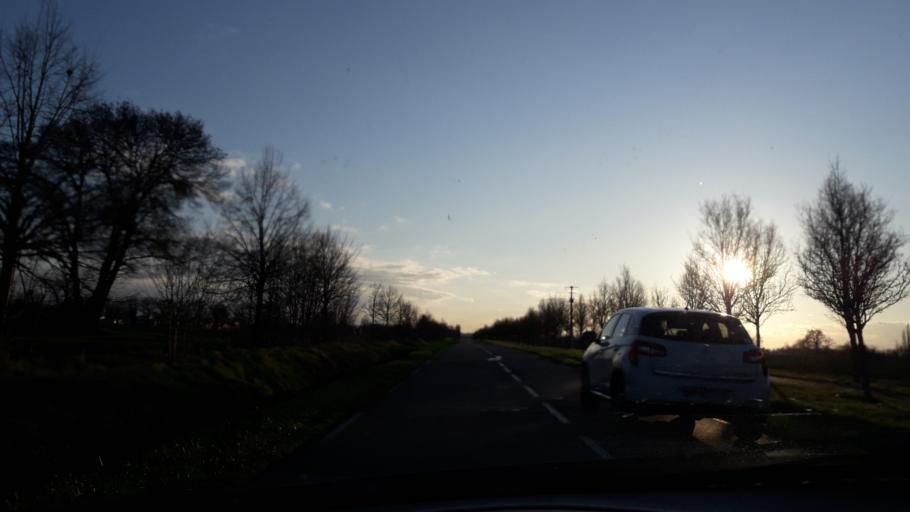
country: FR
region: Midi-Pyrenees
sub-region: Departement de la Haute-Garonne
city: Levignac
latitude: 43.6488
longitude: 1.1691
